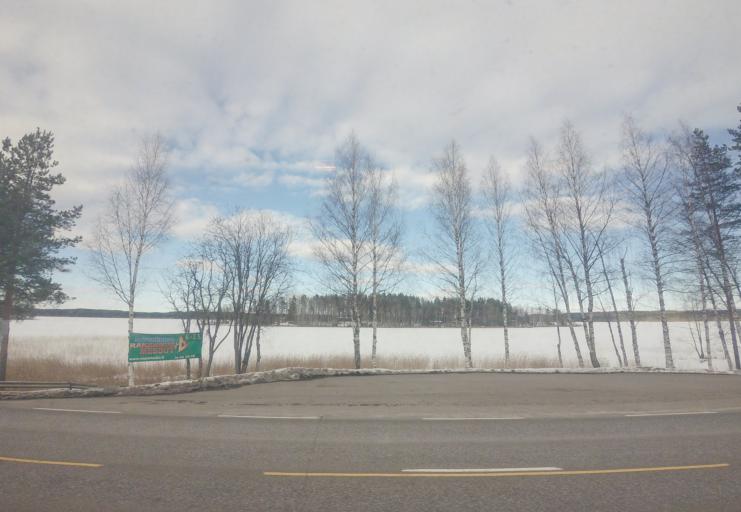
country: FI
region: Southern Savonia
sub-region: Savonlinna
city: Kerimaeki
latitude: 61.8134
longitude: 29.2641
